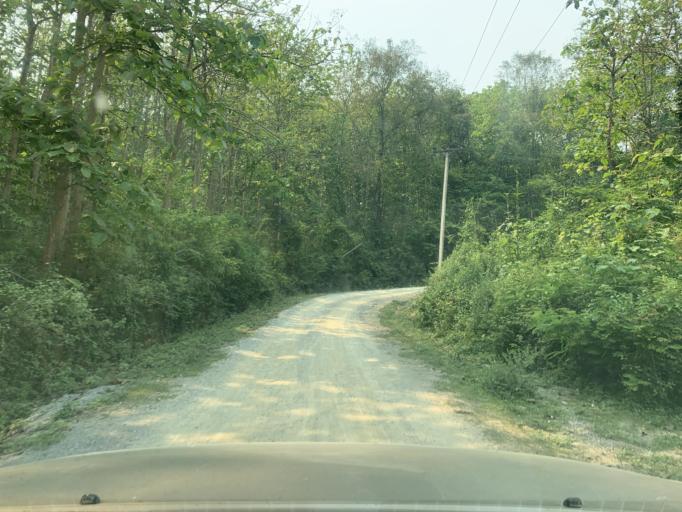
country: LA
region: Louangphabang
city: Louangphabang
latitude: 19.8880
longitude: 102.2516
